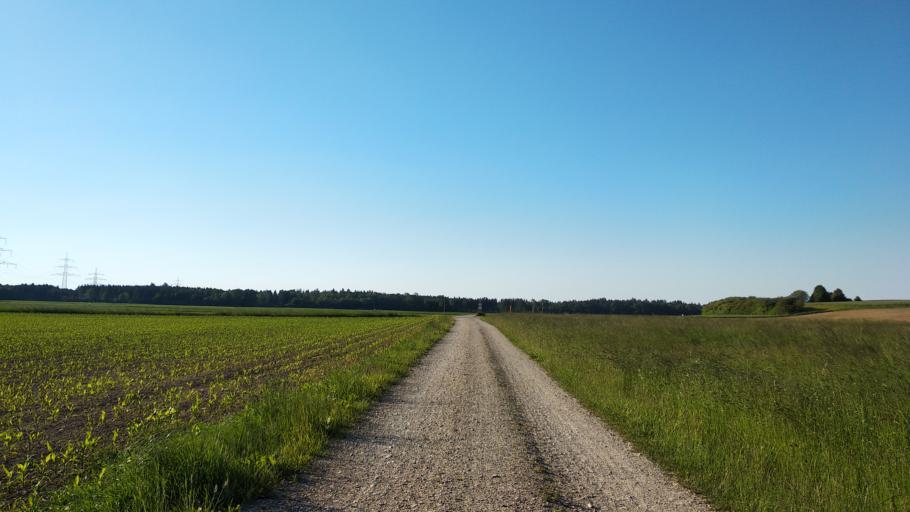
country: DE
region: Bavaria
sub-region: Upper Bavaria
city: Zorneding
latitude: 48.0998
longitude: 11.8185
